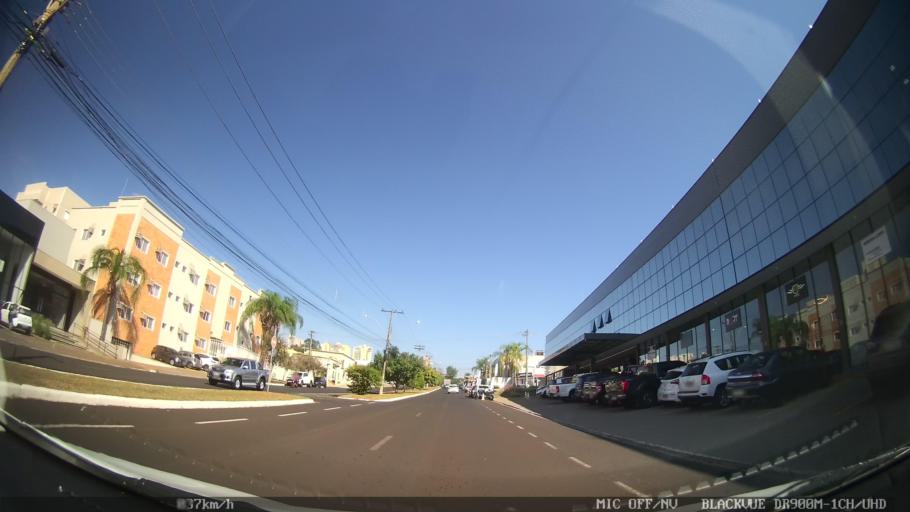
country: BR
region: Sao Paulo
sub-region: Ribeirao Preto
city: Ribeirao Preto
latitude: -21.1997
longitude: -47.8014
